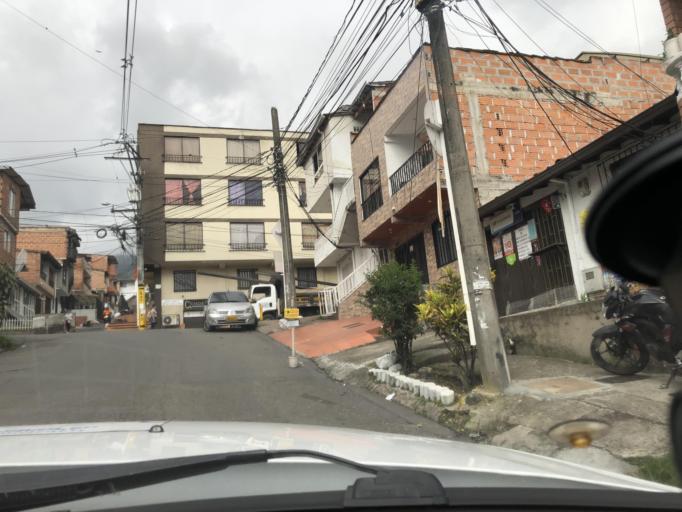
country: CO
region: Antioquia
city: Bello
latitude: 6.3136
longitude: -75.5709
